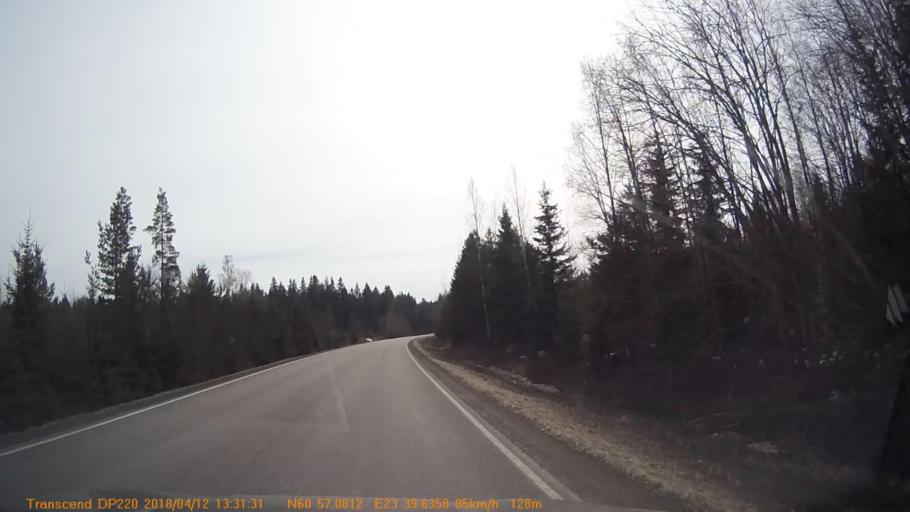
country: FI
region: Haeme
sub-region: Forssa
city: Forssa
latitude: 60.9512
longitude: 23.6606
